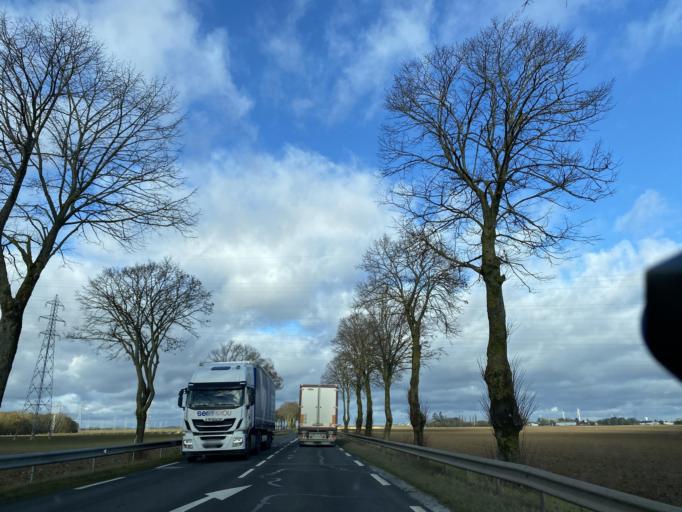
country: FR
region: Centre
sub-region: Departement du Loiret
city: Artenay
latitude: 48.1031
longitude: 1.8646
